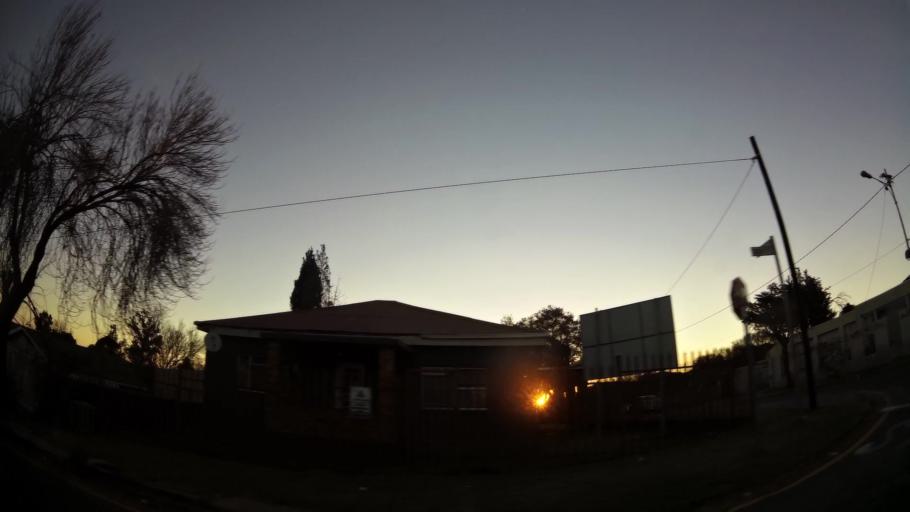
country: ZA
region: Gauteng
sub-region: City of Johannesburg Metropolitan Municipality
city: Roodepoort
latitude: -26.1734
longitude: 27.9148
